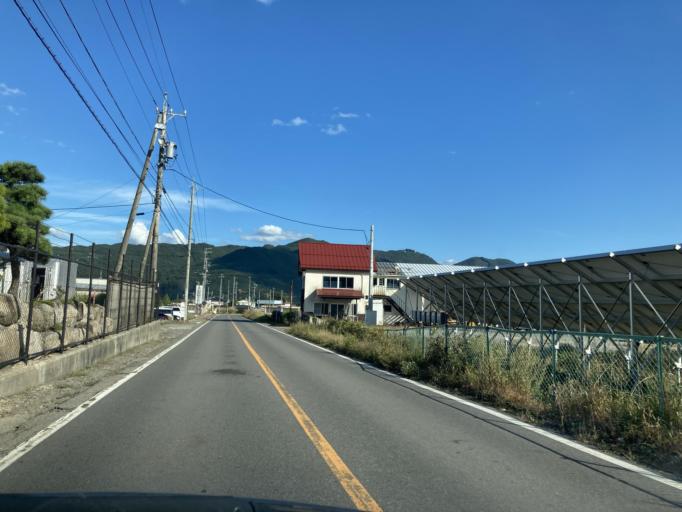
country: JP
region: Nagano
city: Omachi
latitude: 36.5226
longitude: 137.8424
